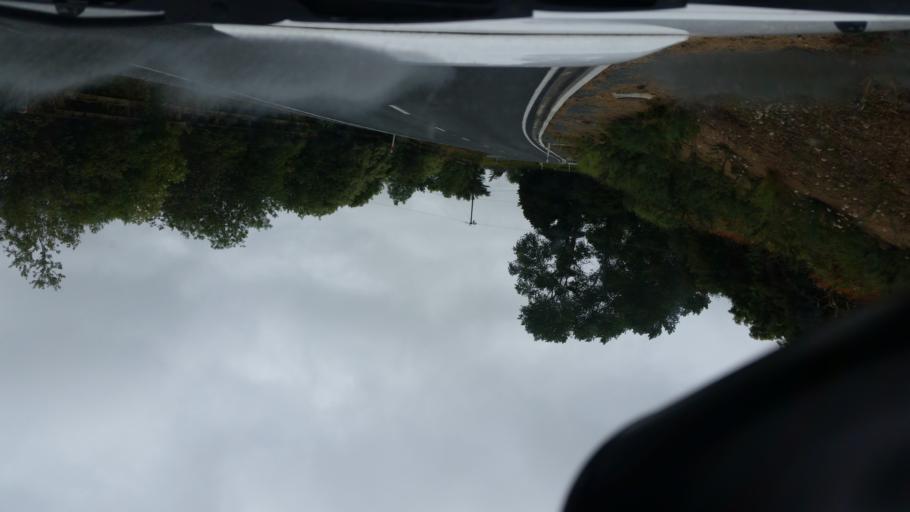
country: NZ
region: Auckland
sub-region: Auckland
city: Wellsford
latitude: -36.1717
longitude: 174.4589
